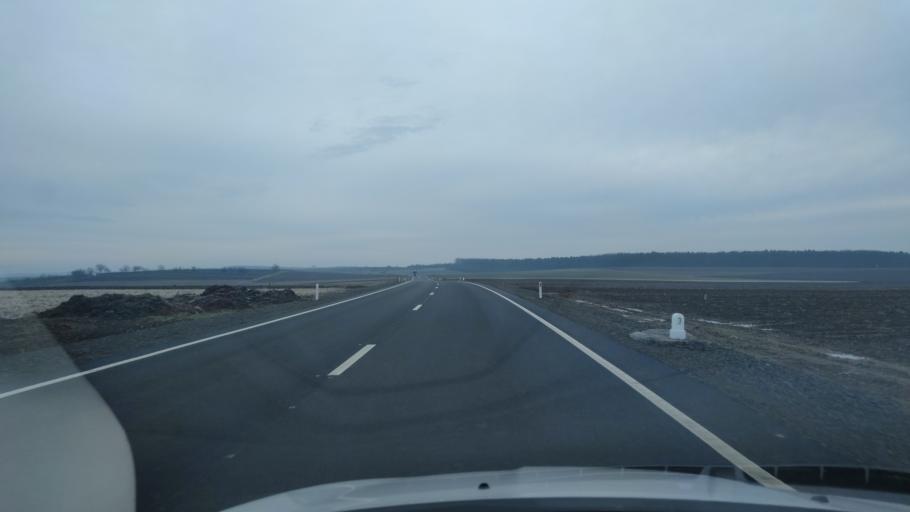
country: RO
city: Szekelyhid
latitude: 47.3353
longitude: 22.1068
